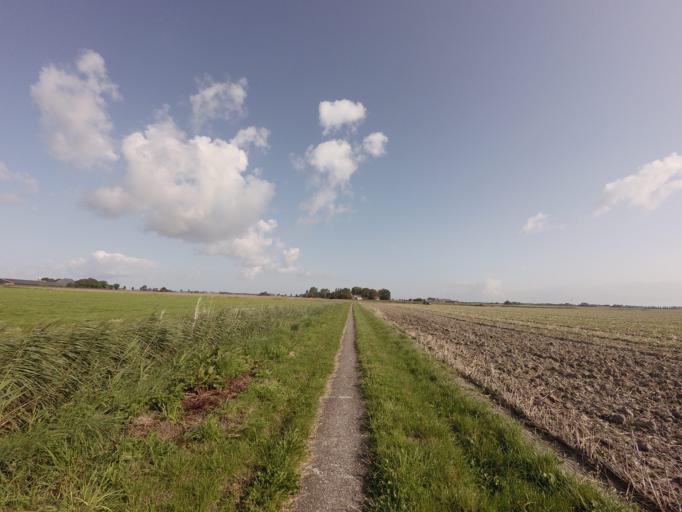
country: NL
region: Friesland
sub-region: Gemeente Franekeradeel
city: Franeker
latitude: 53.2069
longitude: 5.5648
